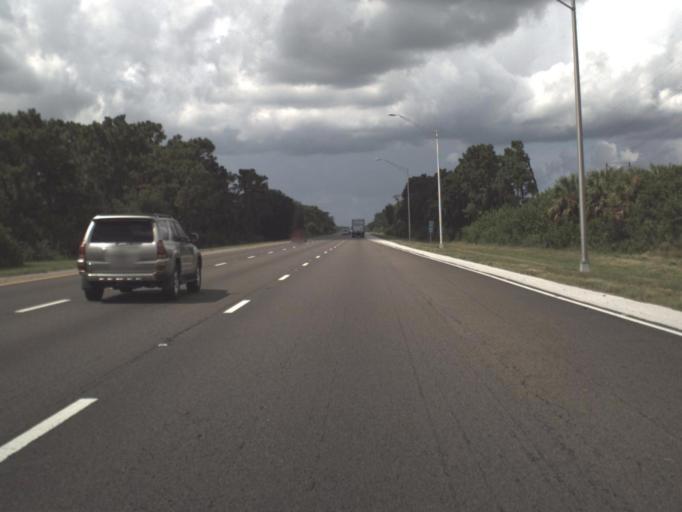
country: US
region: Florida
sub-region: Hillsborough County
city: Ruskin
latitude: 27.6848
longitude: -82.4222
